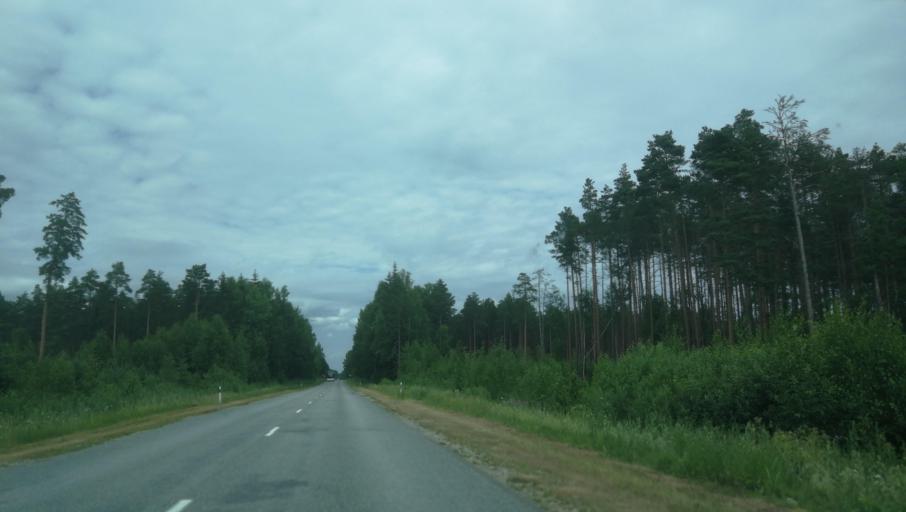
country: LV
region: Valmieras Rajons
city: Valmiera
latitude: 57.7002
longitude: 25.4277
